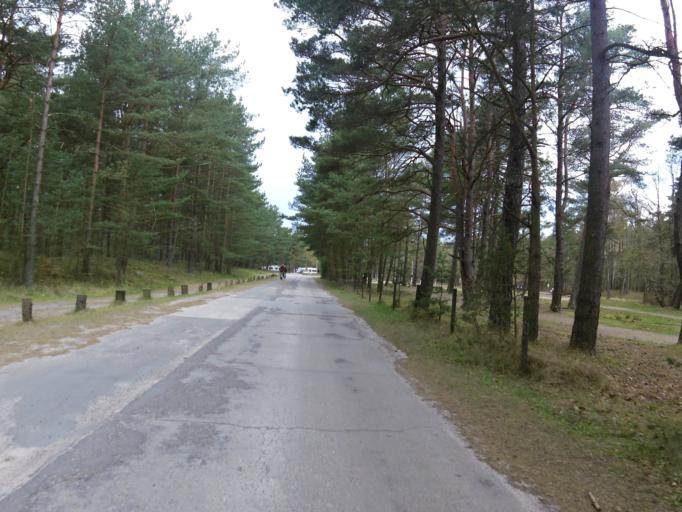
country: DE
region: Mecklenburg-Vorpommern
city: Ostseebad Prerow
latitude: 54.4566
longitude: 12.5401
